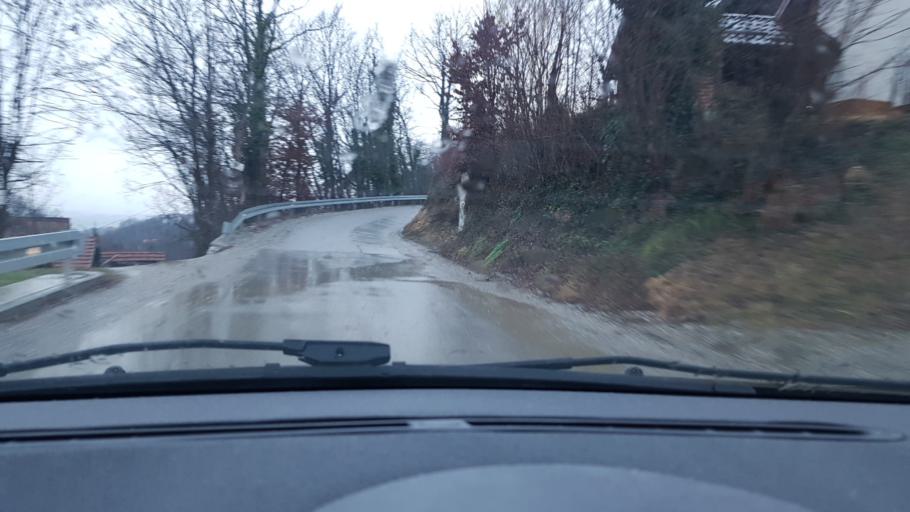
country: HR
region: Krapinsko-Zagorska
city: Bedekovcina
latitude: 45.9964
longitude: 15.9849
